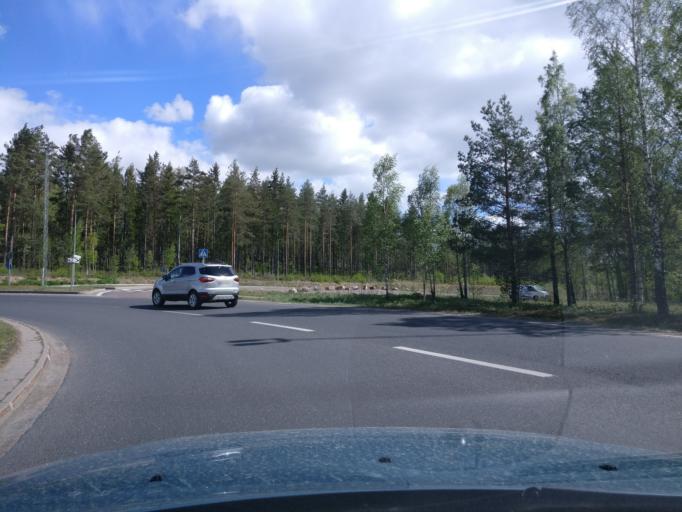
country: SE
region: Vaermland
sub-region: Karlstads Kommun
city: Skattkarr
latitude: 59.3951
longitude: 13.5813
